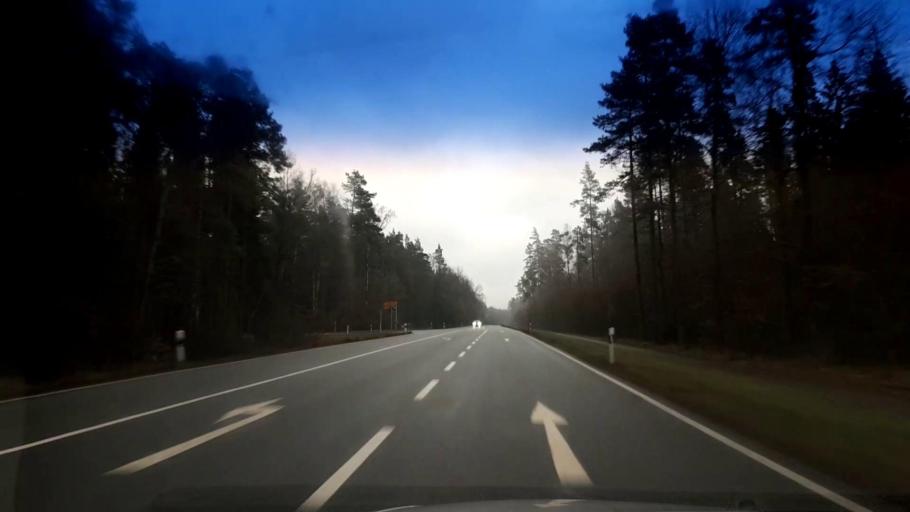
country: DE
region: Bavaria
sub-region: Upper Palatinate
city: Leonberg
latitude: 49.9265
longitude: 12.2810
